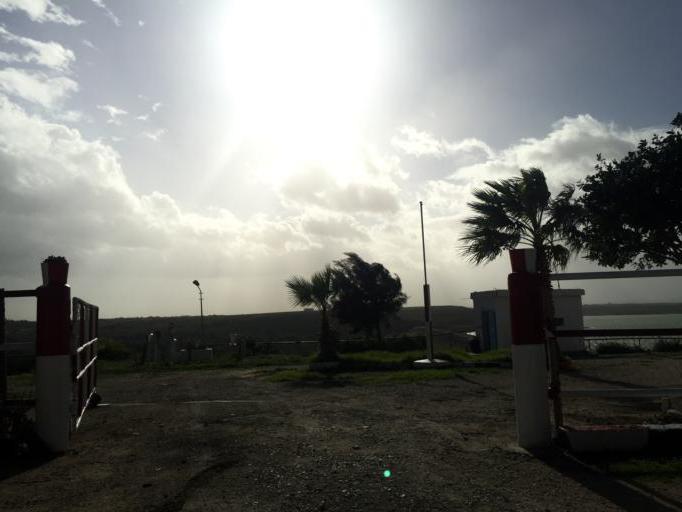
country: TN
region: Nabul
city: Menzel Heurr
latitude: 36.7409
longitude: 10.9248
